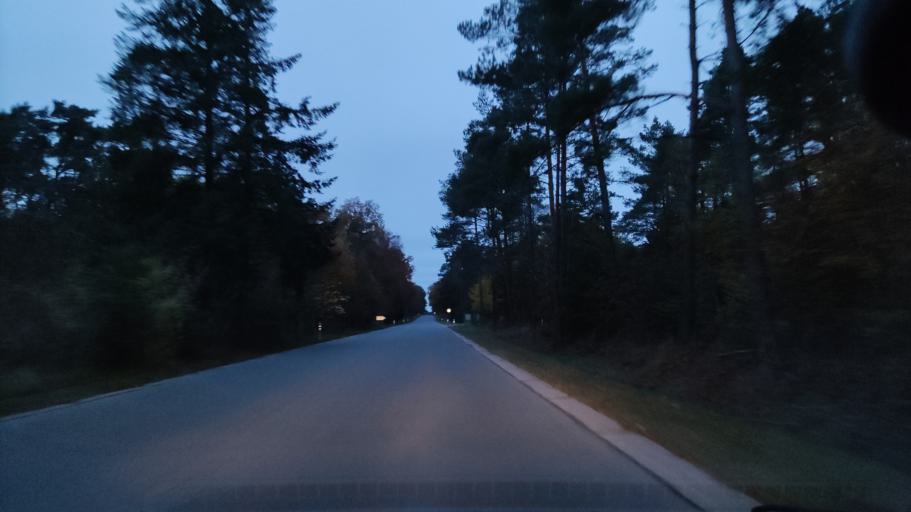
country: DE
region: Lower Saxony
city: Munster
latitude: 53.0063
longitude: 10.1120
